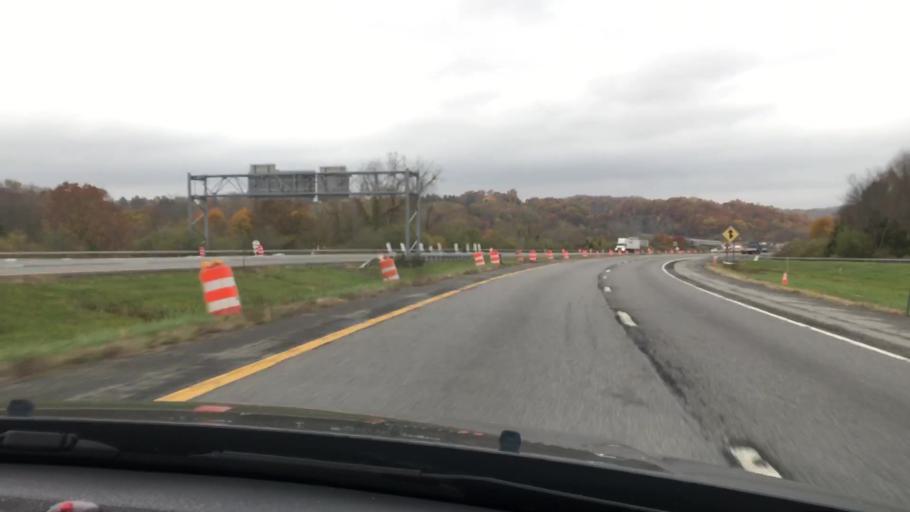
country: US
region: New York
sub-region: Putnam County
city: Brewster
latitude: 41.3928
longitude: -73.5998
